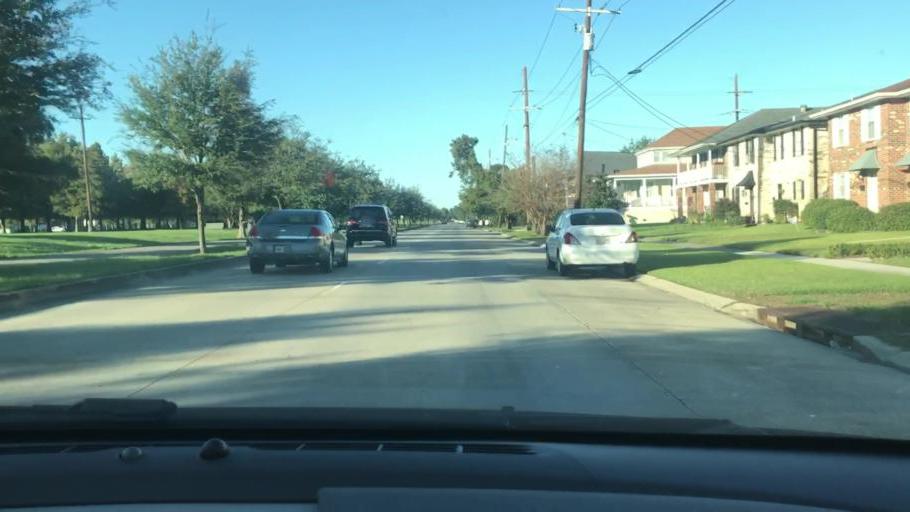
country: US
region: Louisiana
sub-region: Jefferson Parish
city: Metairie
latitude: 30.0071
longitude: -90.1145
